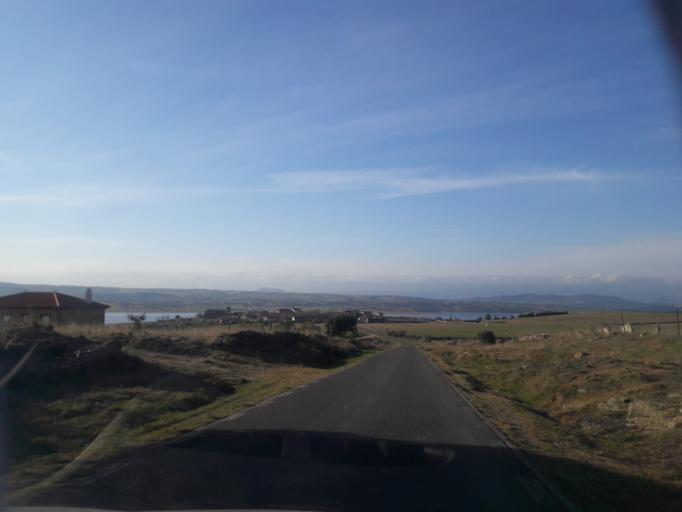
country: ES
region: Castille and Leon
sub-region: Provincia de Salamanca
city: Salvatierra de Tormes
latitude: 40.5963
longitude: -5.5993
